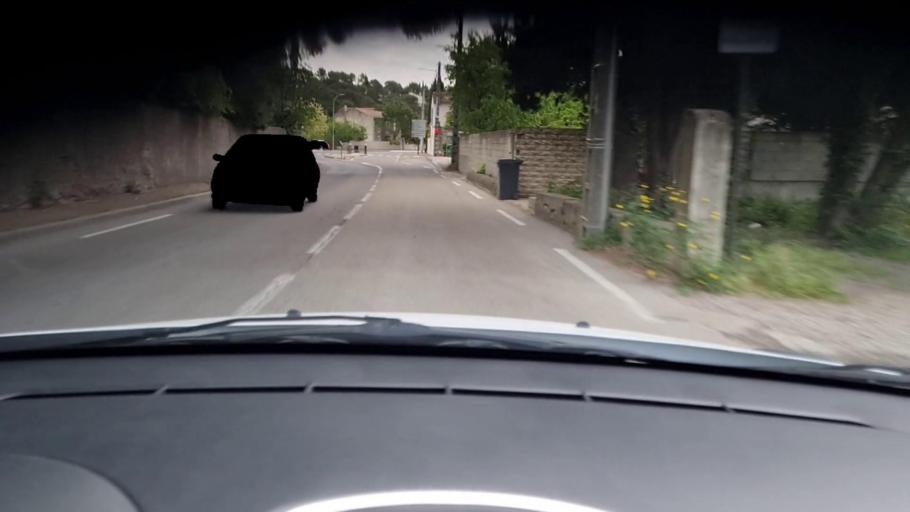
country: FR
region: Languedoc-Roussillon
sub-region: Departement du Gard
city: Nimes
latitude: 43.8560
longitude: 4.3789
